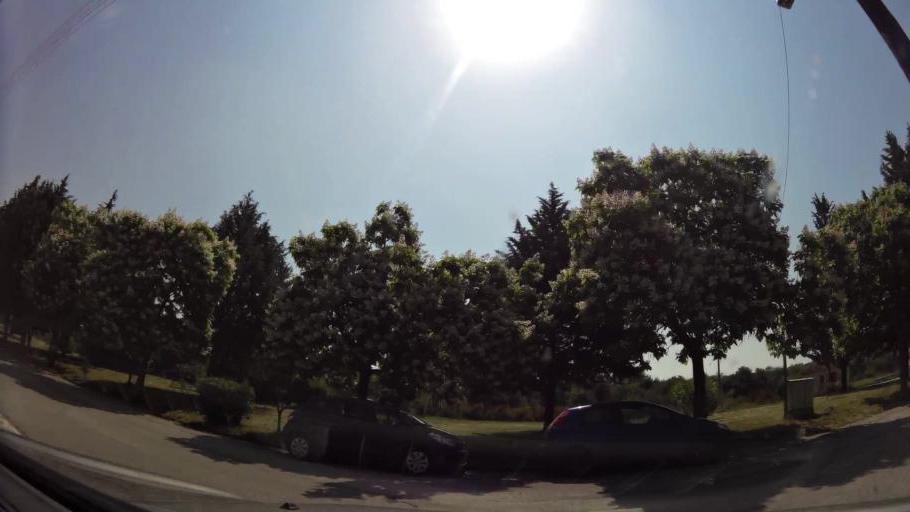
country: GR
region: West Macedonia
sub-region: Nomos Kozanis
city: Koila
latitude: 40.3362
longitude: 21.7915
